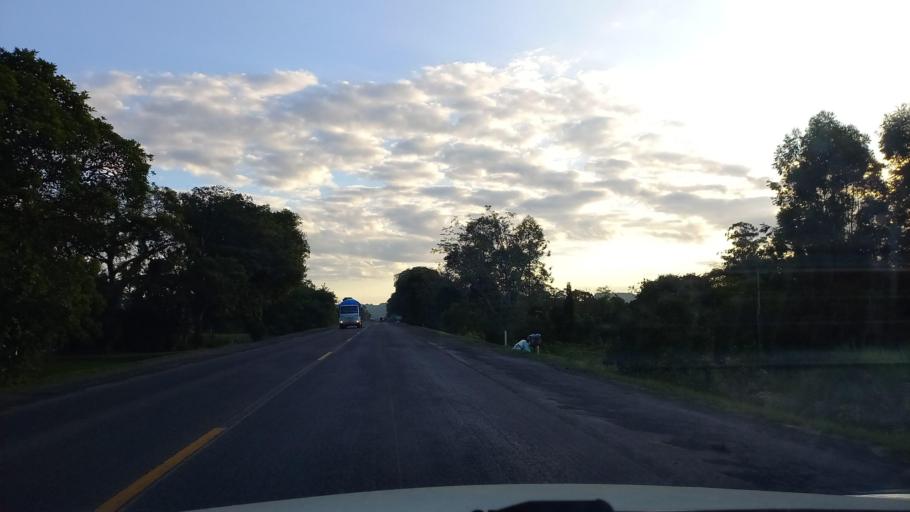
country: BR
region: Rio Grande do Sul
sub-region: Santa Cruz Do Sul
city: Santa Cruz do Sul
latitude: -29.6779
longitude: -52.3166
